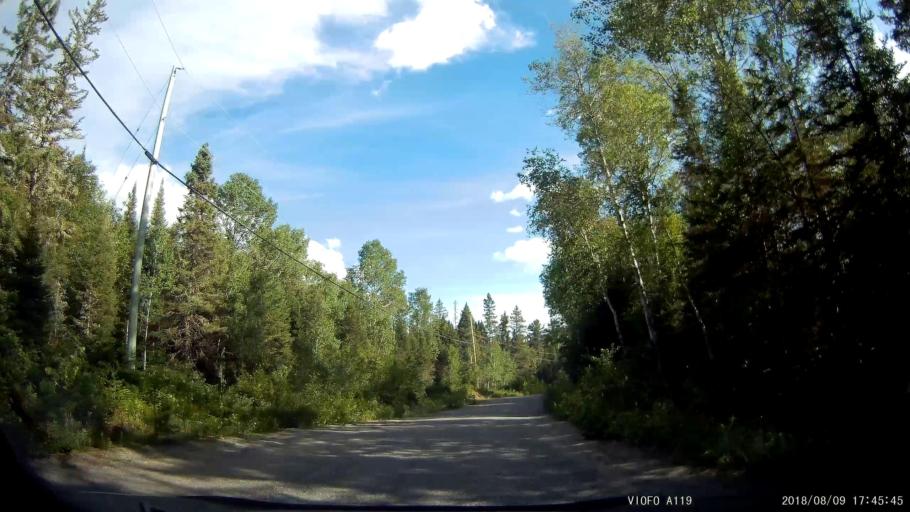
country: CA
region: Ontario
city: Rayside-Balfour
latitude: 46.5984
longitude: -81.5340
